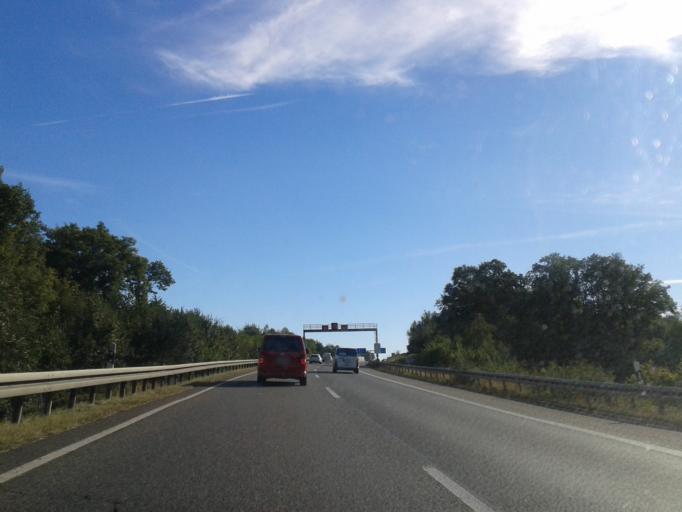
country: DE
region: Saxony
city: Albertstadt
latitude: 51.1370
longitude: 13.7507
